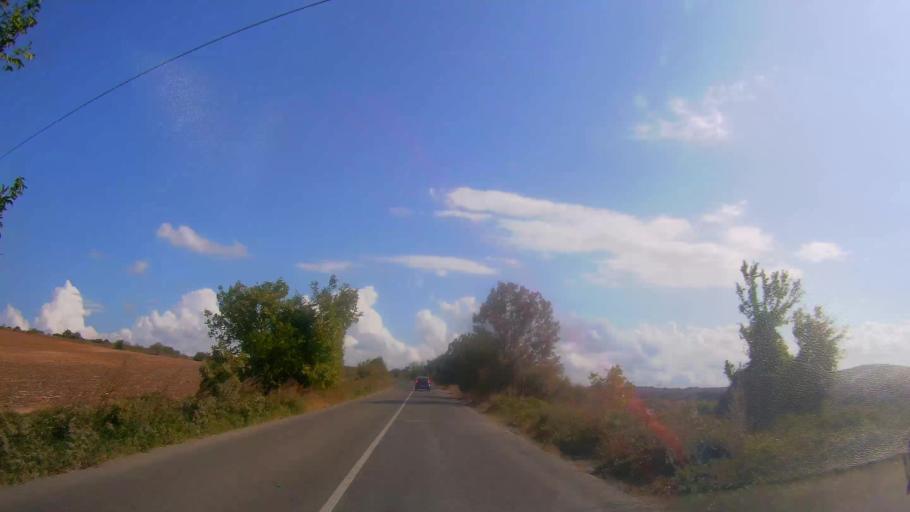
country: BG
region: Burgas
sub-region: Obshtina Burgas
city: Burgas
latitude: 42.4787
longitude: 27.3890
